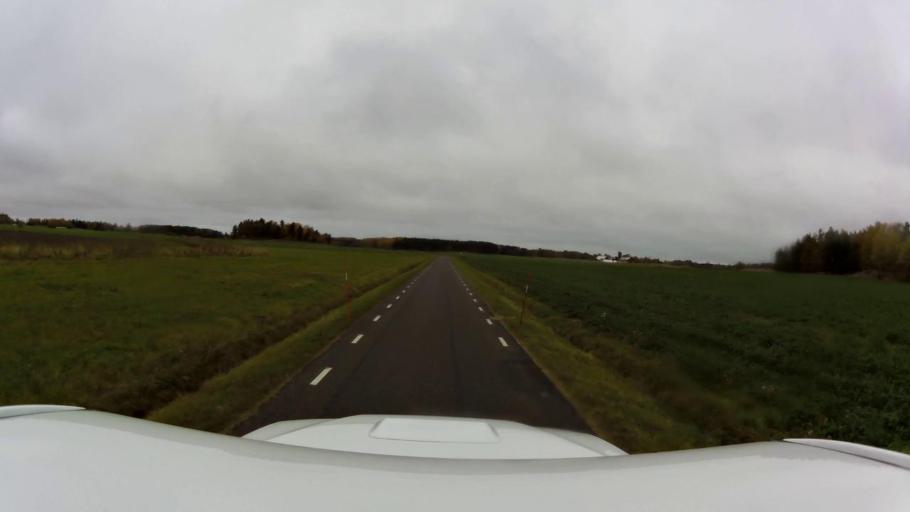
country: SE
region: OEstergoetland
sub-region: Linkopings Kommun
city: Linghem
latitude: 58.4842
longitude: 15.8137
